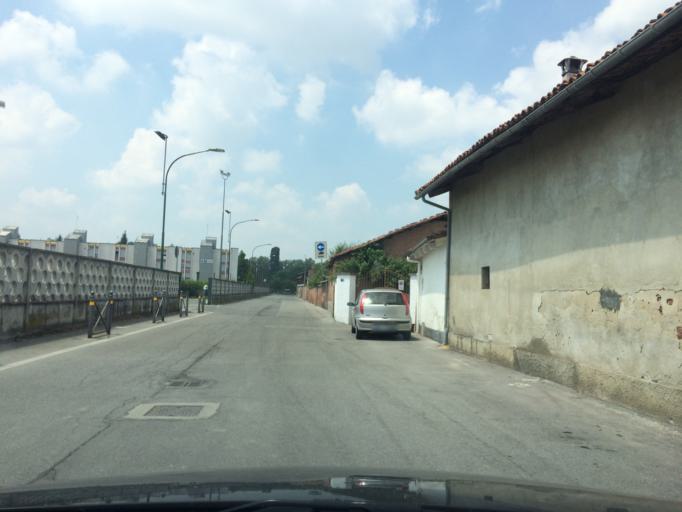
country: IT
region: Piedmont
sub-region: Provincia di Cuneo
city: Racconigi
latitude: 44.7655
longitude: 7.6715
